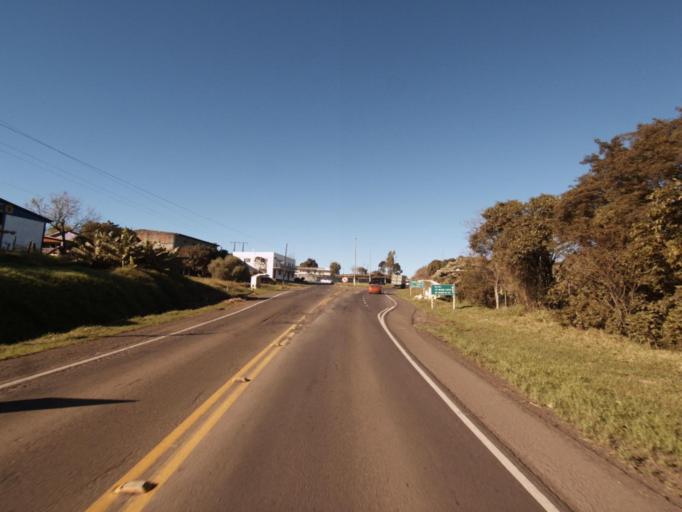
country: AR
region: Misiones
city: Bernardo de Irigoyen
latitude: -26.6548
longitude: -53.5173
